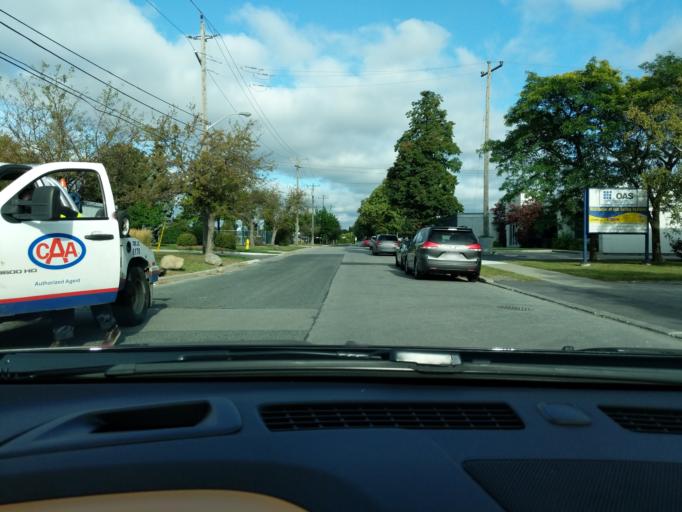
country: CA
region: Ontario
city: Toronto
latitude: 43.7203
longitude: -79.4656
